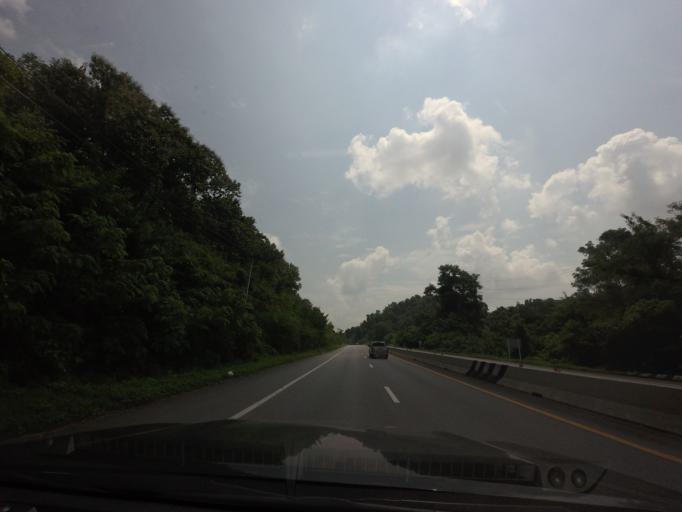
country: TH
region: Uttaradit
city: Lap Lae
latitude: 17.7795
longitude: 100.1222
